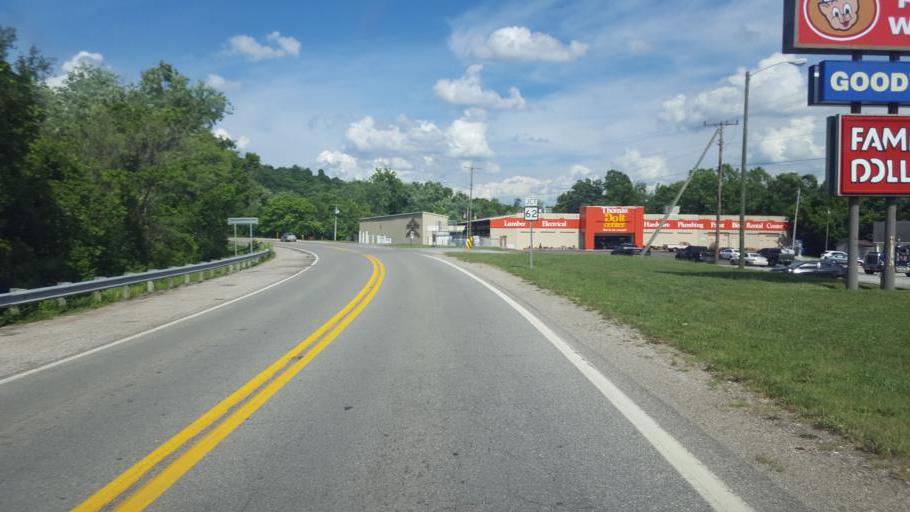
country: US
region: West Virginia
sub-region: Mason County
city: Point Pleasant
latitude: 38.8411
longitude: -82.1370
